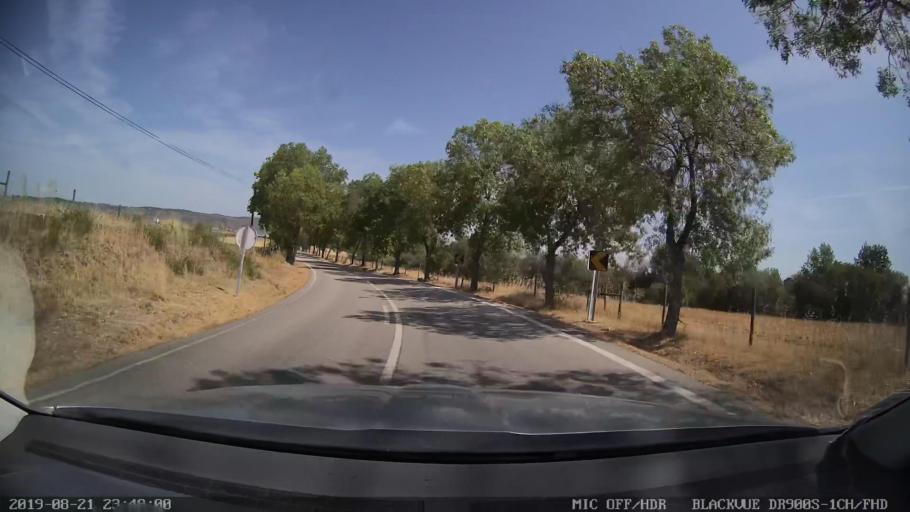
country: PT
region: Castelo Branco
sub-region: Idanha-A-Nova
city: Idanha-a-Nova
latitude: 39.8726
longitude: -7.2518
